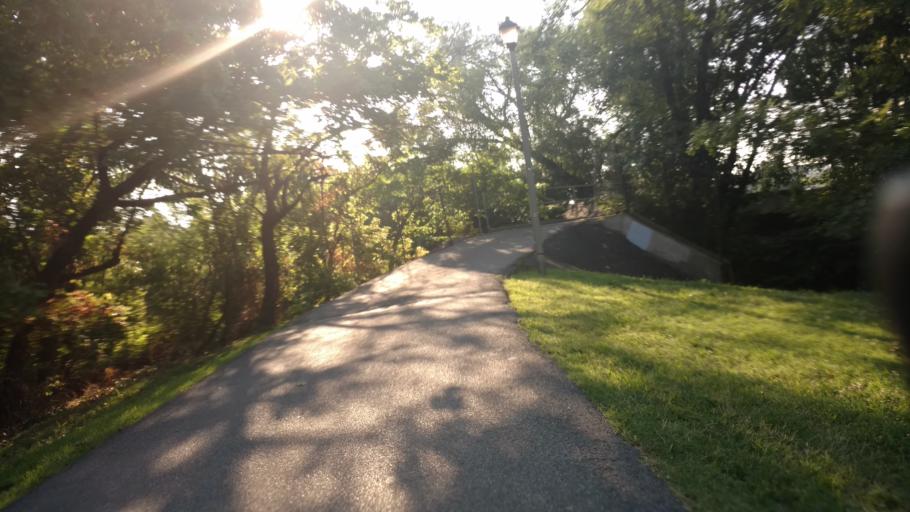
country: US
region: Virginia
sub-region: City of Alexandria
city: Alexandria
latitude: 38.8400
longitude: -77.0584
